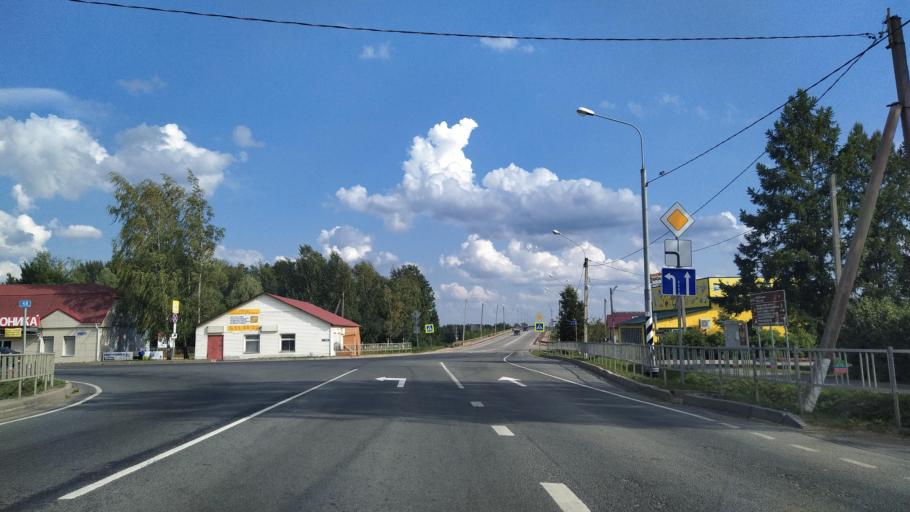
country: RU
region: Novgorod
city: Shimsk
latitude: 58.2095
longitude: 30.7188
